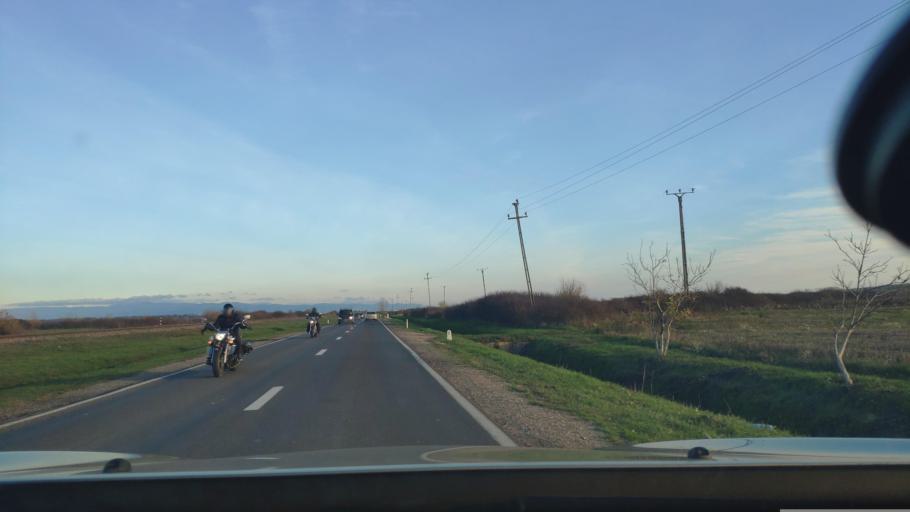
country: RO
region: Satu Mare
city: Culciu Mic
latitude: 47.7898
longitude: 23.0415
